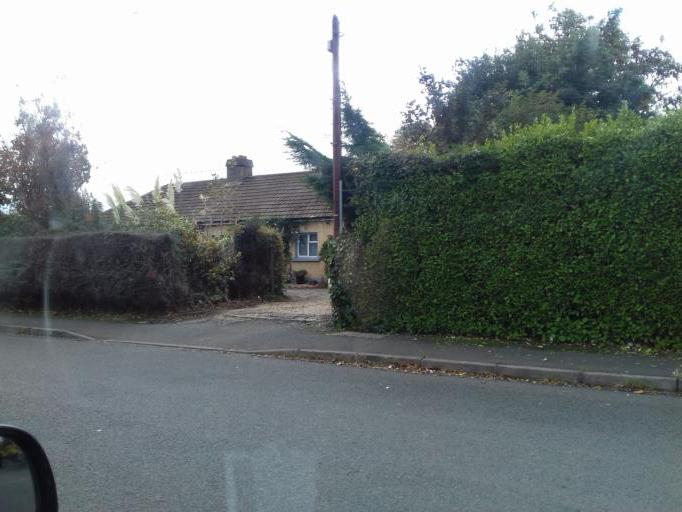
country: IE
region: Leinster
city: Little Bray
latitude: 53.1889
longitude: -6.1293
